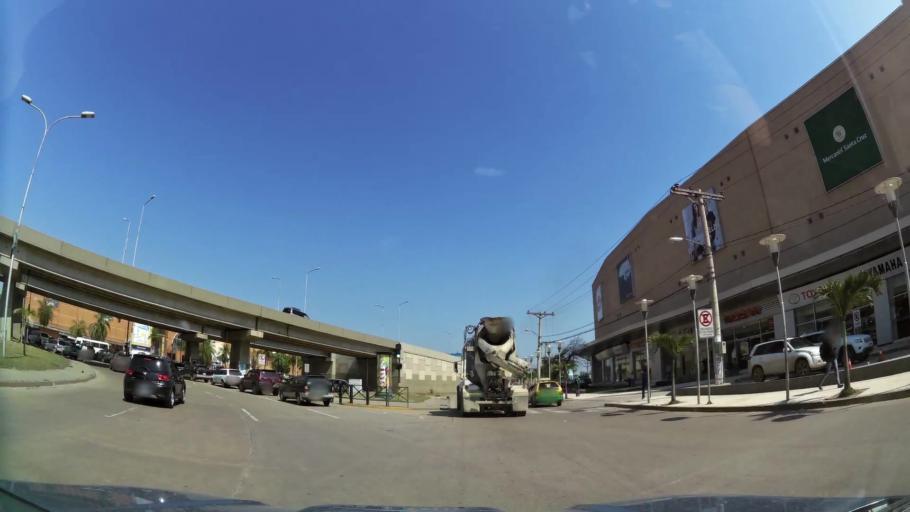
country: BO
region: Santa Cruz
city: Santa Cruz de la Sierra
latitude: -17.7495
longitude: -63.1756
